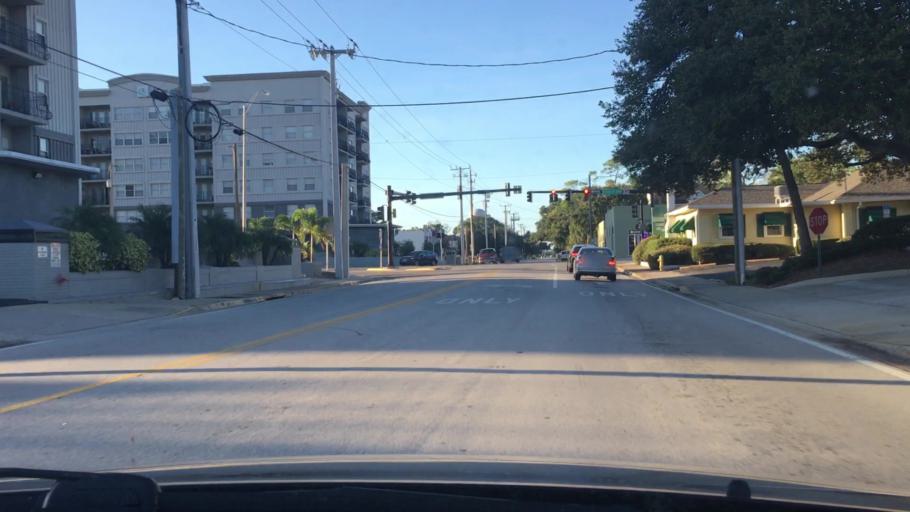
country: US
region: Florida
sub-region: Volusia County
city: Holly Hill
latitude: 29.2329
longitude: -81.0178
